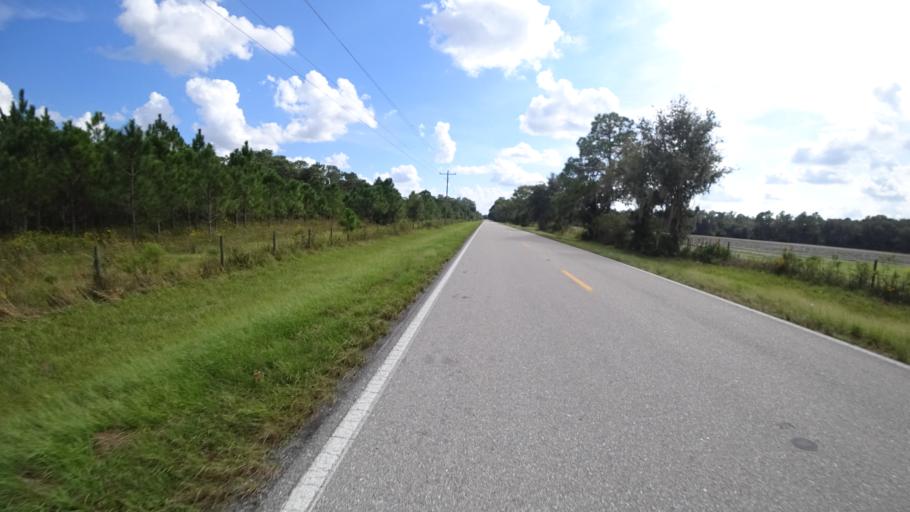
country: US
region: Florida
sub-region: Hillsborough County
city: Wimauma
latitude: 27.5690
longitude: -82.1046
